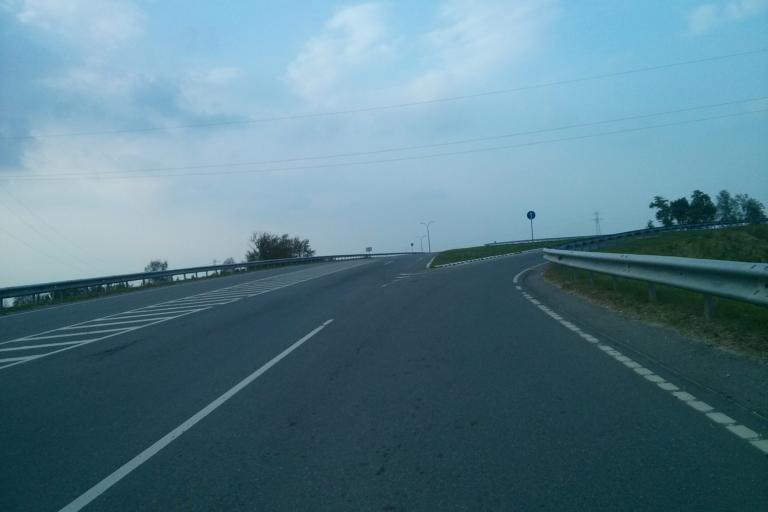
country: BY
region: Minsk
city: Chervyen'
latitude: 53.7216
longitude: 28.3955
